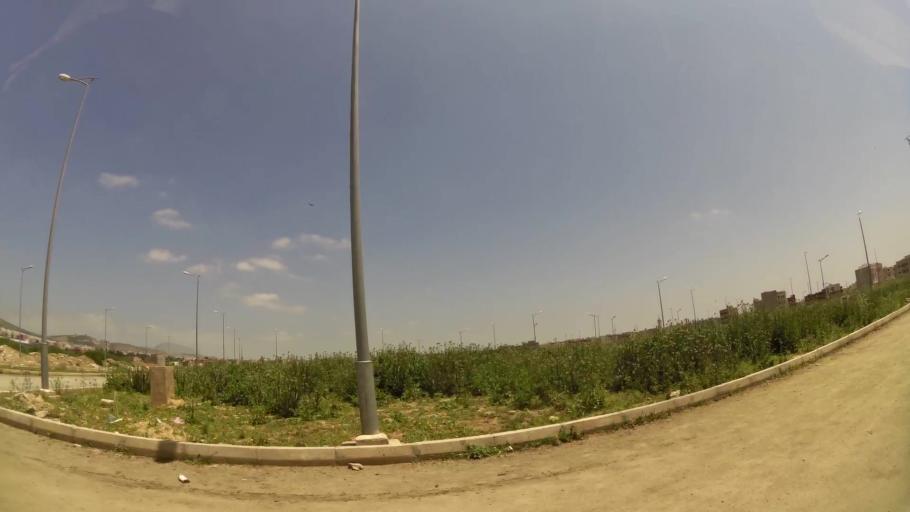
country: MA
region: Fes-Boulemane
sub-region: Fes
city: Fes
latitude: 34.0386
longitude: -5.0573
